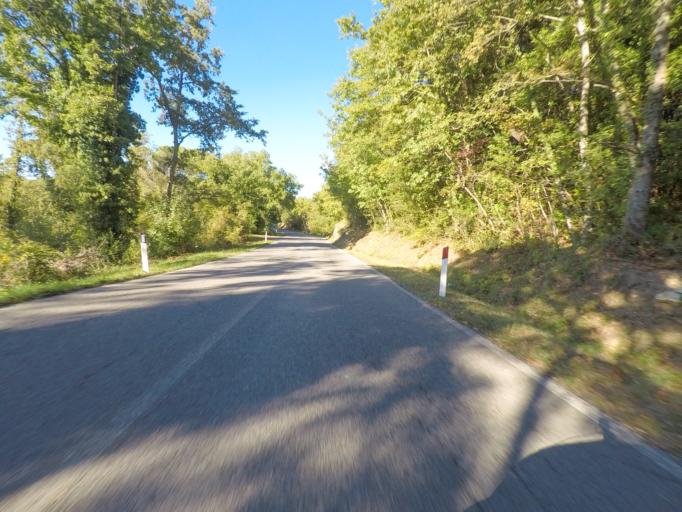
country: IT
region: Tuscany
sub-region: Provincia di Siena
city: Belverde
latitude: 43.3863
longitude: 11.3448
